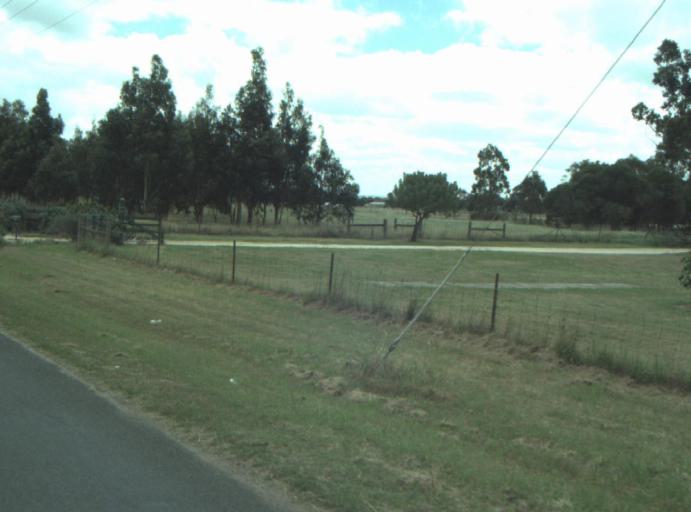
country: AU
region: Victoria
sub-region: Greater Geelong
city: Breakwater
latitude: -38.2078
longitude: 144.3661
